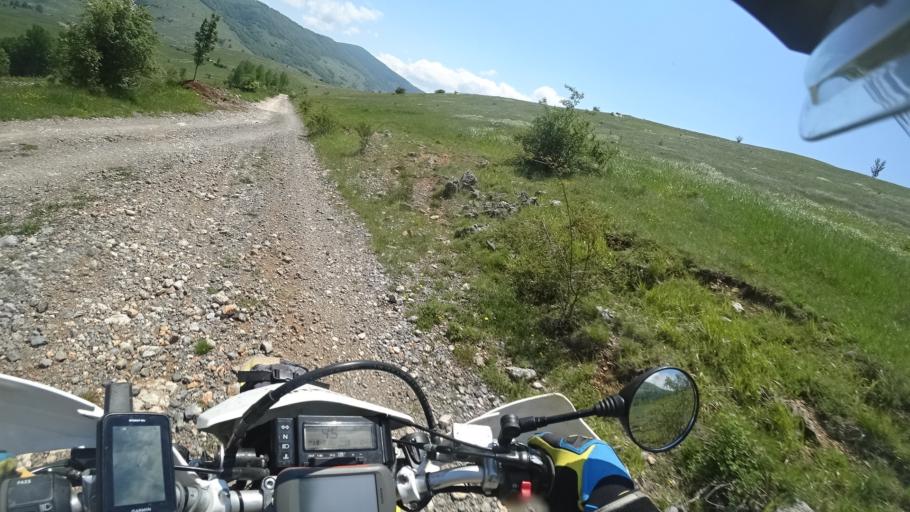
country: HR
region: Zadarska
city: Gracac
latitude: 44.4407
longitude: 15.9181
